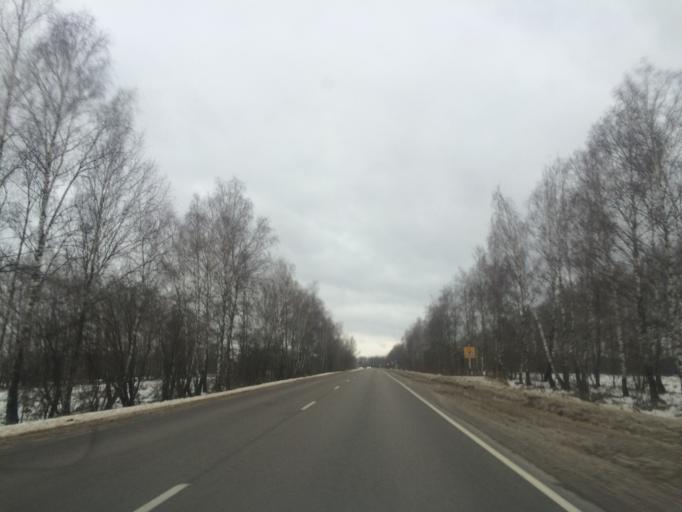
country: RU
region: Tula
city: Leninskiy
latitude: 54.1316
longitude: 37.3085
